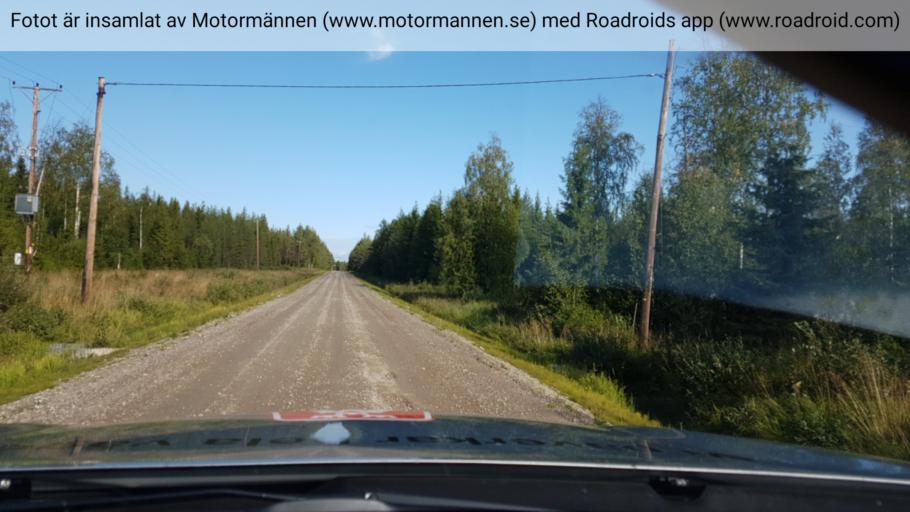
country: SE
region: Norrbotten
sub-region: Kalix Kommun
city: Kalix
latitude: 66.1490
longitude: 23.2239
